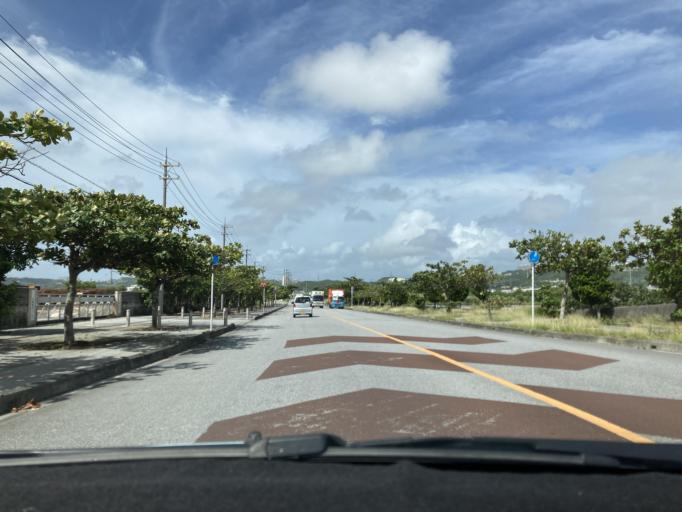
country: JP
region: Okinawa
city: Ginowan
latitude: 26.2196
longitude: 127.7772
